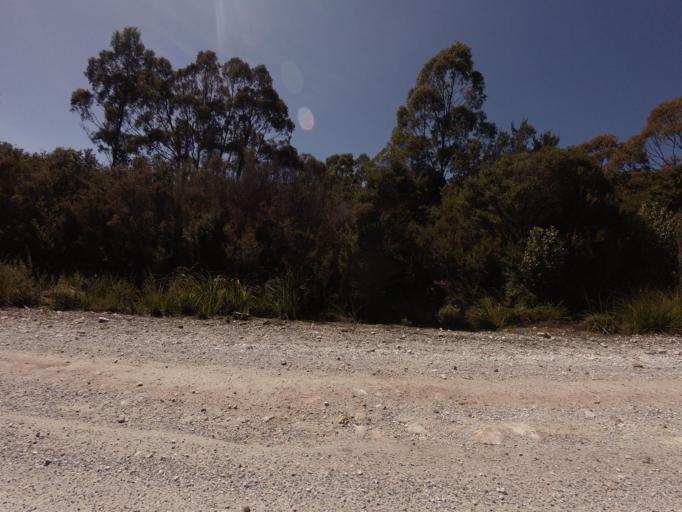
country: AU
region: Tasmania
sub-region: Huon Valley
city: Geeveston
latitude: -43.0157
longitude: 146.3656
